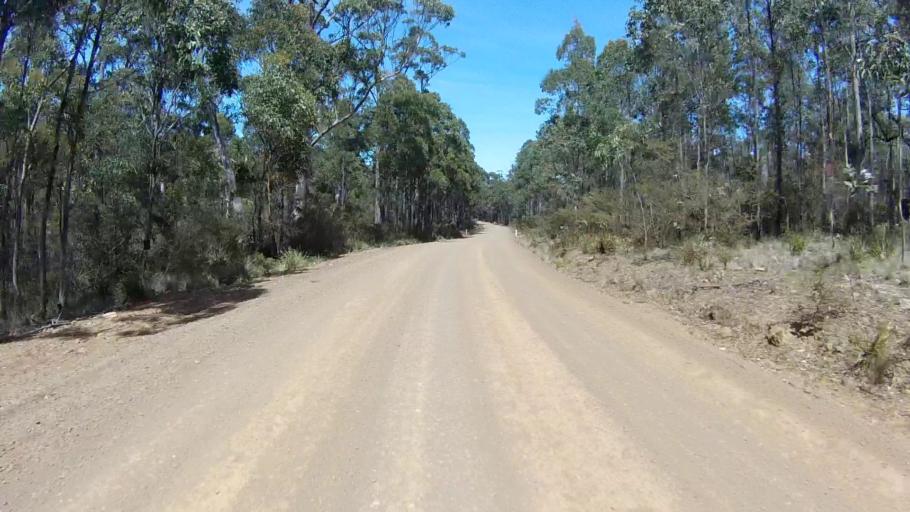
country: AU
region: Tasmania
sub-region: Sorell
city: Sorell
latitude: -42.6699
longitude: 147.7293
